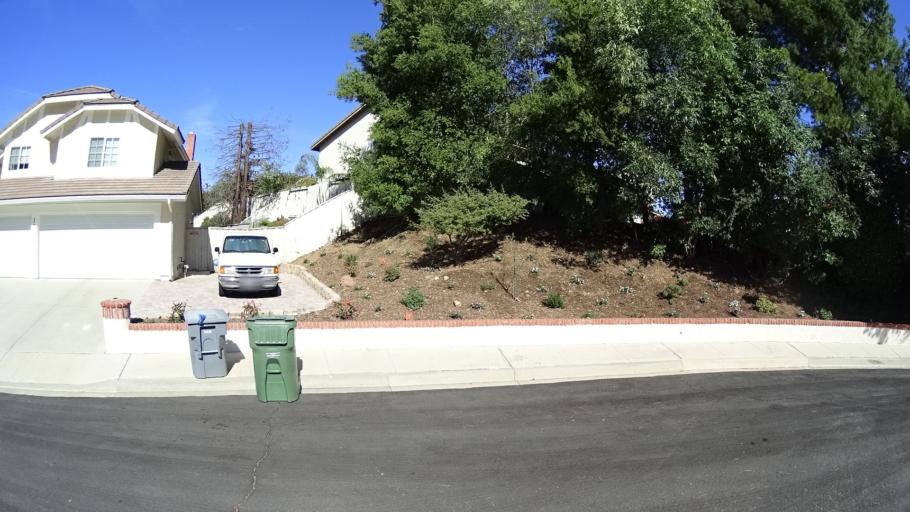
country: US
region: California
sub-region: Ventura County
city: Thousand Oaks
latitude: 34.2279
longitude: -118.8556
